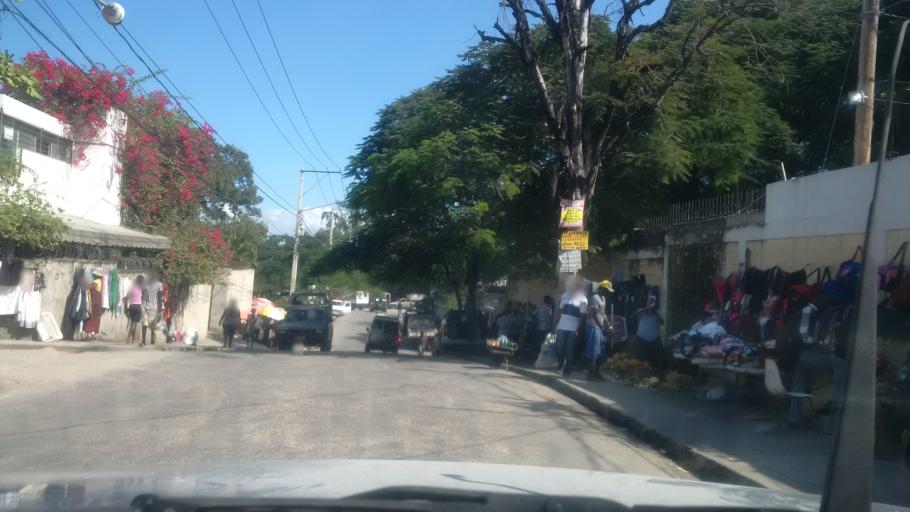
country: HT
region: Ouest
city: Delmas 73
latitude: 18.5348
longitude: -72.2909
